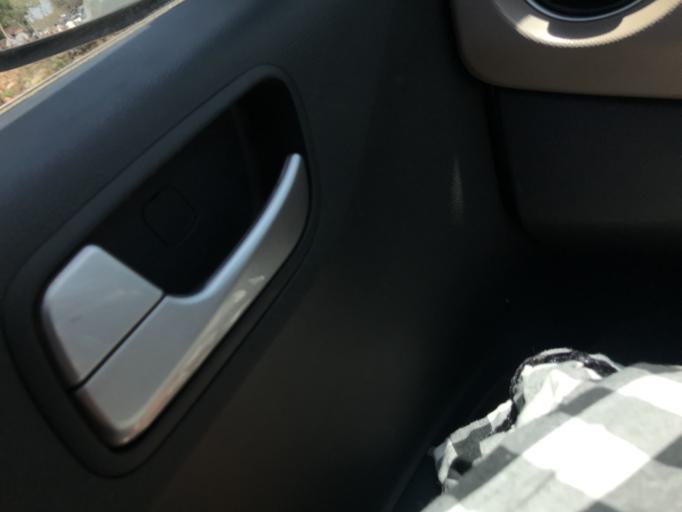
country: IN
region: Telangana
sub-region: Medak
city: Serilingampalle
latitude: 17.4671
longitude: 78.3322
